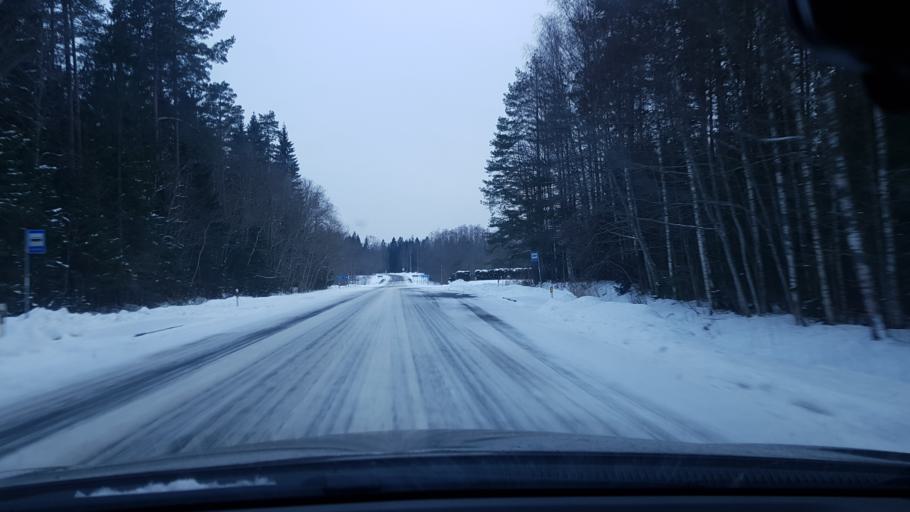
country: EE
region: Harju
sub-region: Loksa linn
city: Loksa
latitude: 59.5521
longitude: 25.7897
